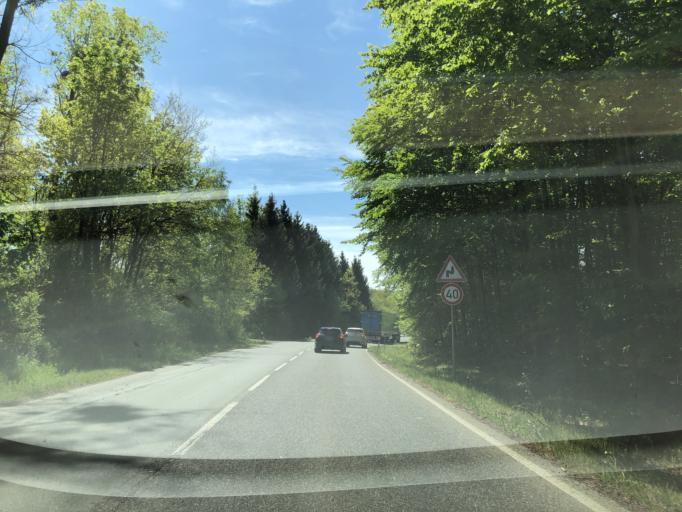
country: DE
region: Hesse
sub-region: Regierungsbezirk Kassel
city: Homberg
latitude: 51.0522
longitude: 9.4339
